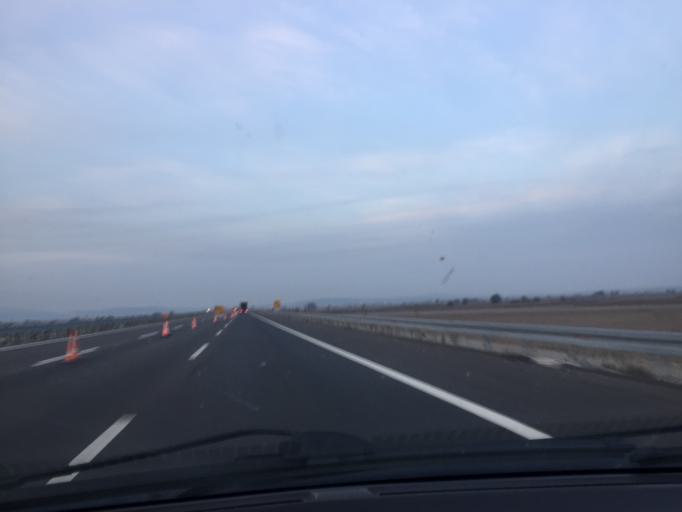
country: TR
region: Manisa
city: Halitpasa
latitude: 38.7197
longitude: 27.6513
